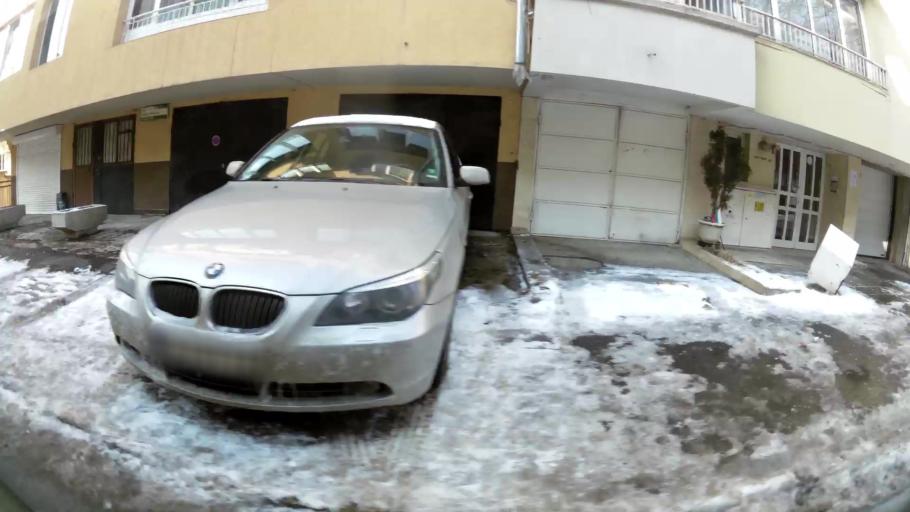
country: BG
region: Sofia-Capital
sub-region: Stolichna Obshtina
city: Sofia
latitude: 42.6723
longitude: 23.3161
